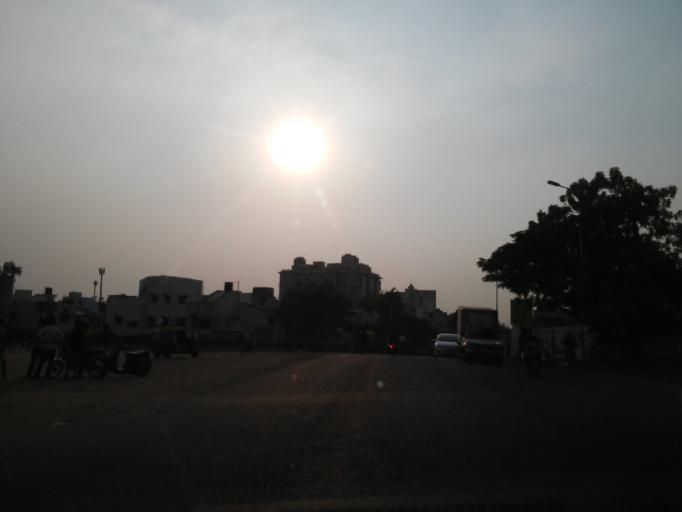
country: IN
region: Gujarat
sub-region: Ahmadabad
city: Sarkhej
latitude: 23.0157
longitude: 72.5361
